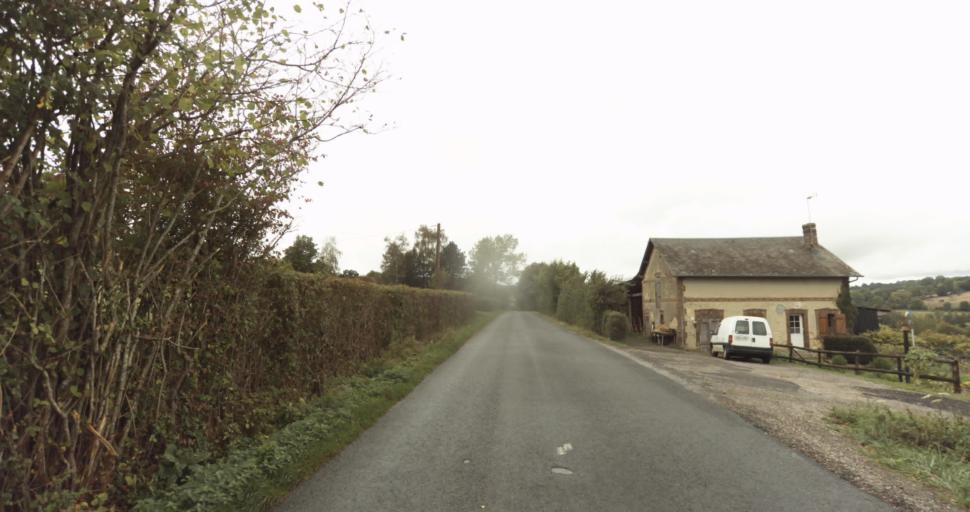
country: FR
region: Lower Normandy
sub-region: Departement de l'Orne
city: Vimoutiers
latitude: 48.8856
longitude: 0.2144
